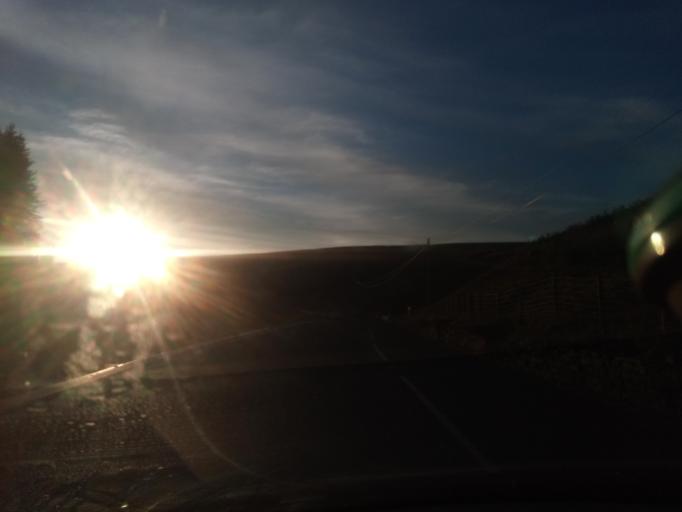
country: GB
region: England
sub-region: County Durham
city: Holwick
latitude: 54.7837
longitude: -2.2735
